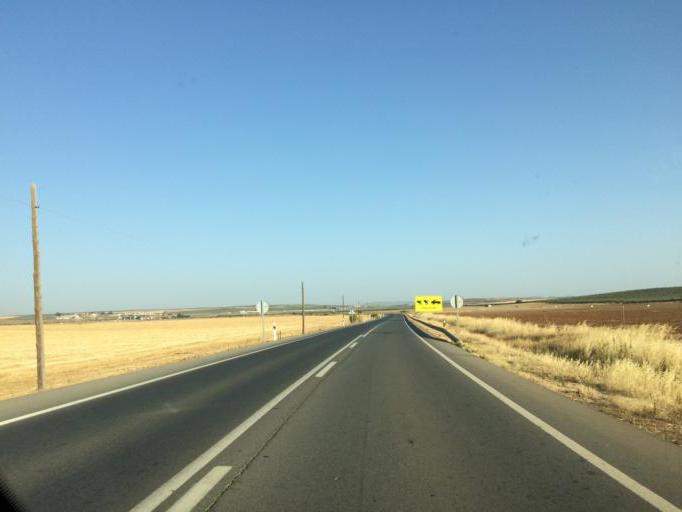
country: ES
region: Andalusia
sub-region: Provincia de Malaga
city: Humilladero
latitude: 37.0598
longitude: -4.6924
